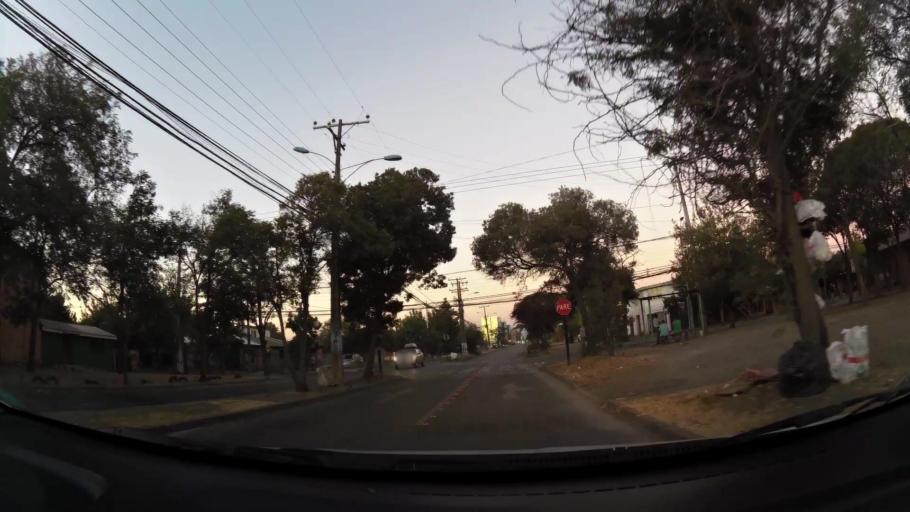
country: CL
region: O'Higgins
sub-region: Provincia de Cachapoal
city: Rancagua
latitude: -34.1837
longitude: -70.7313
